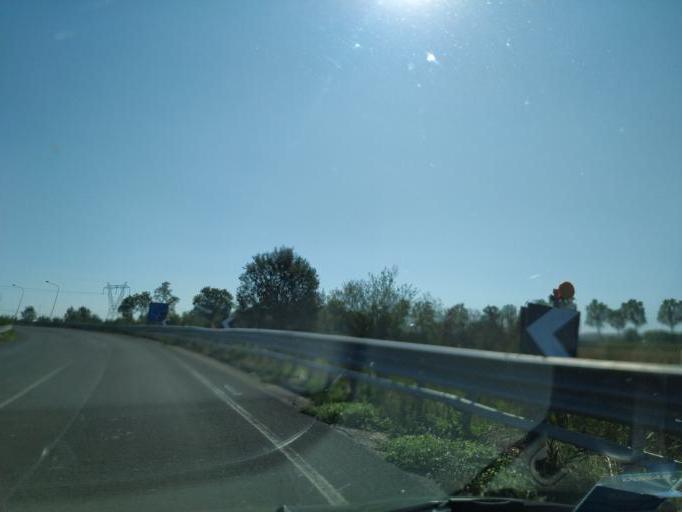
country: IT
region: Emilia-Romagna
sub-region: Provincia di Bologna
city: Decima
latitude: 44.6740
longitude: 11.2083
